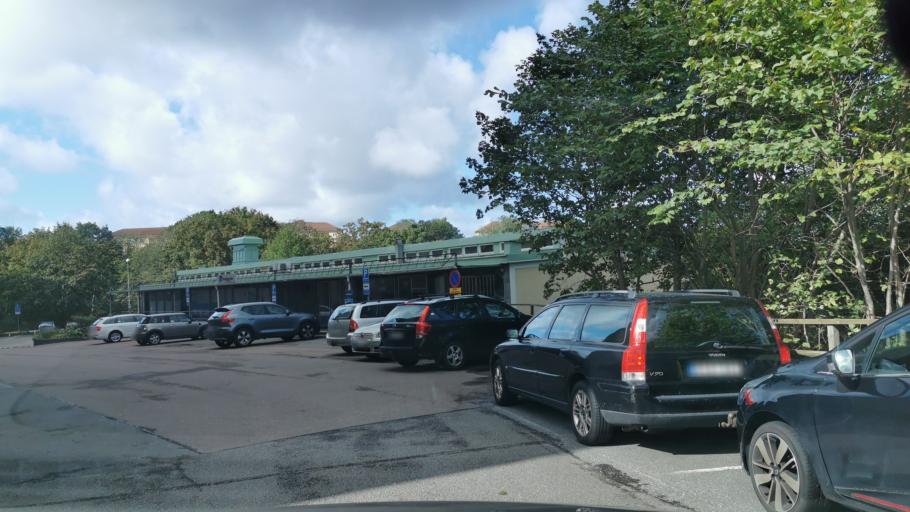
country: SE
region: Vaestra Goetaland
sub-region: Goteborg
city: Majorna
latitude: 57.6896
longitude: 11.9319
